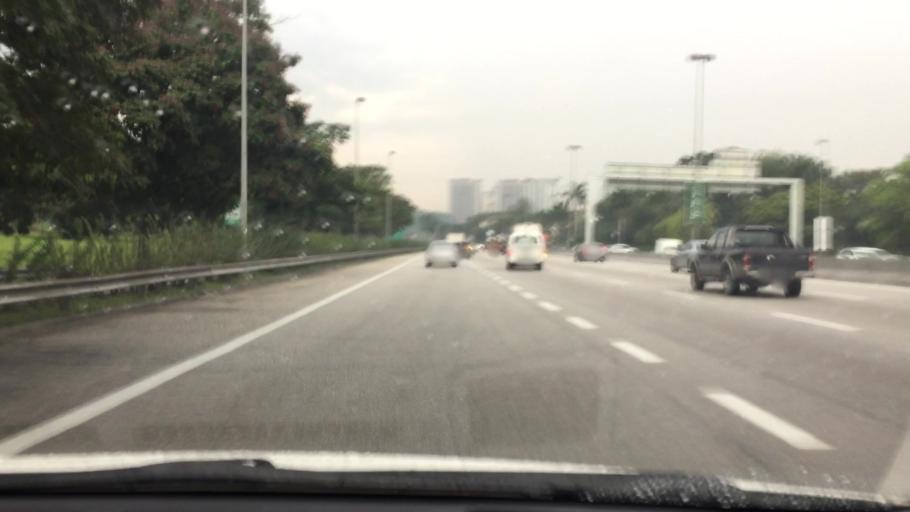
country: MY
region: Selangor
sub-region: Petaling
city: Petaling Jaya
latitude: 3.0688
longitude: 101.6386
